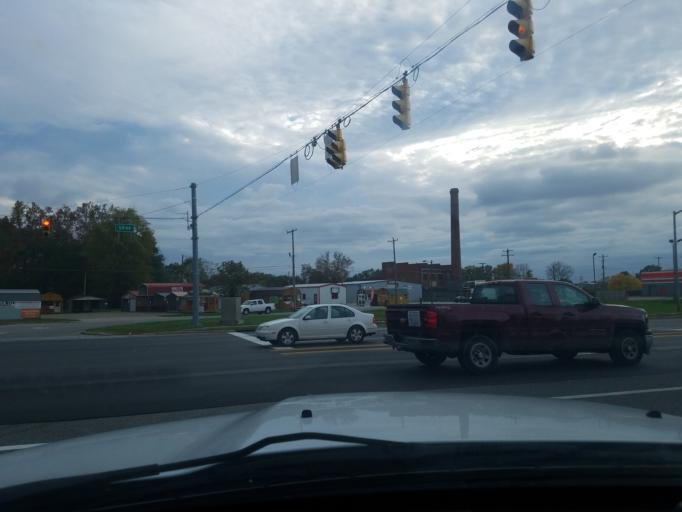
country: US
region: Indiana
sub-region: Shelby County
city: Shelbyville
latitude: 39.5231
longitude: -85.7677
